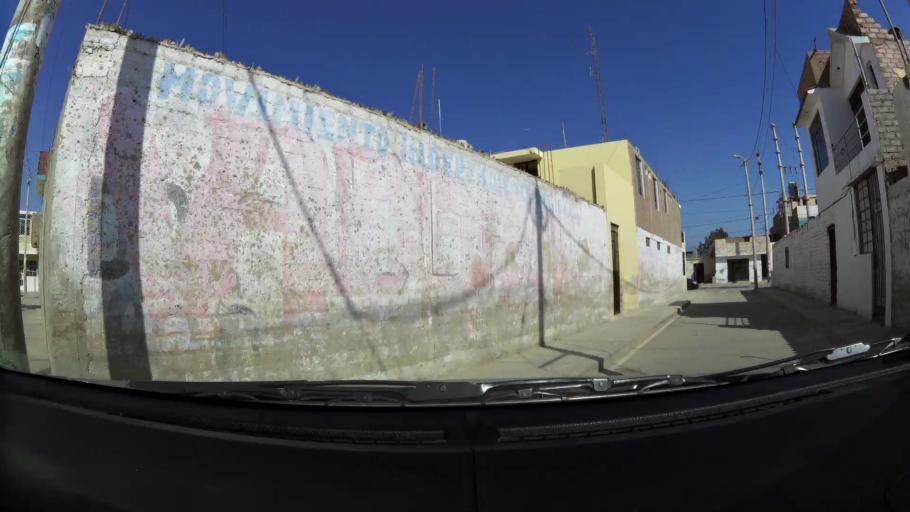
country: PE
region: Ancash
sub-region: Provincia de Huarmey
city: Huarmey
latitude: -10.0705
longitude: -78.1546
